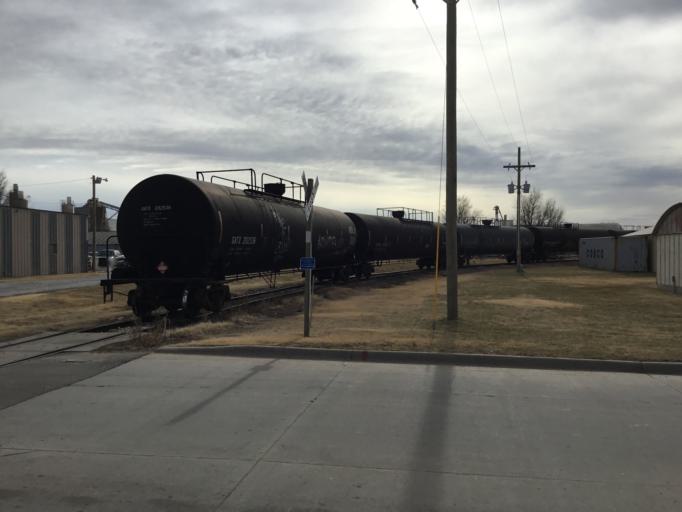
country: US
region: Kansas
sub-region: McPherson County
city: McPherson
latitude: 38.3737
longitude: -97.6801
